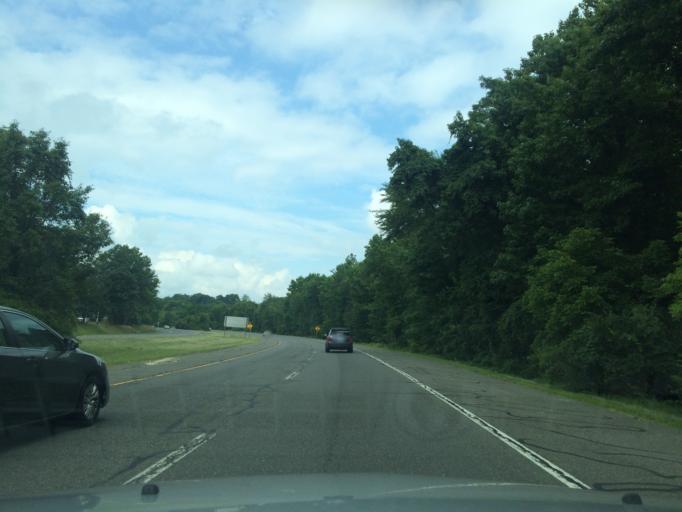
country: US
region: Maryland
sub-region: Prince George's County
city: Coral Hills
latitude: 38.8659
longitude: -76.9271
